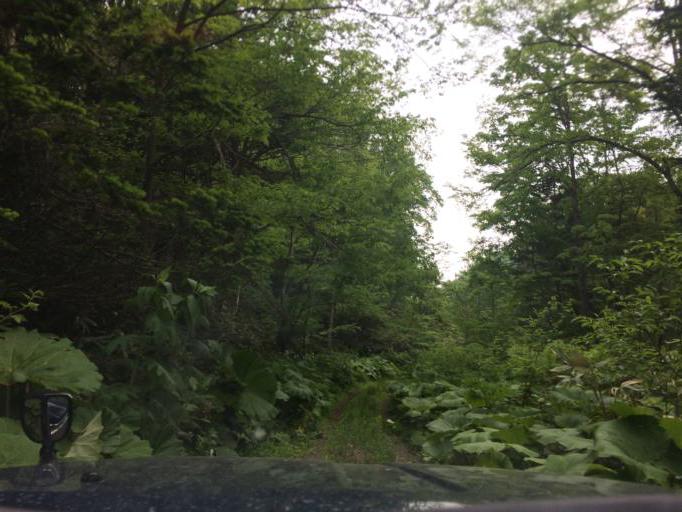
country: JP
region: Hokkaido
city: Niseko Town
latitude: 42.6344
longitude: 140.5766
